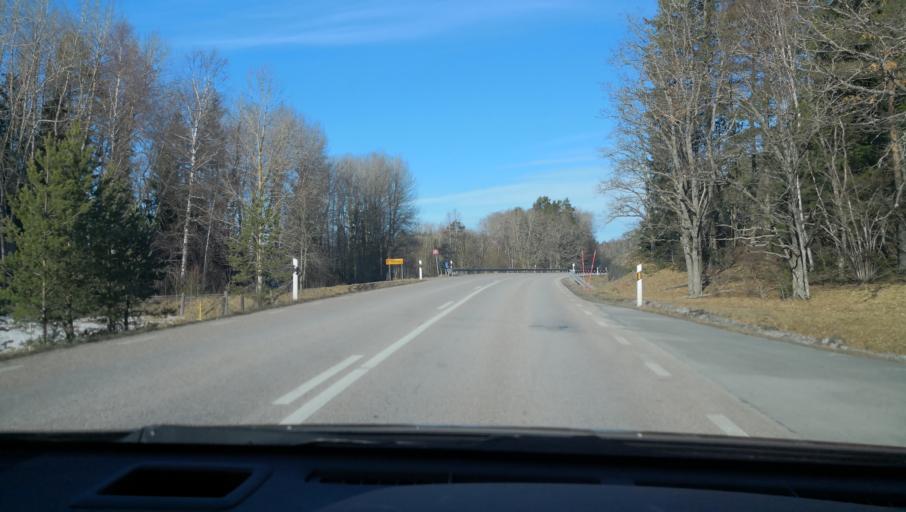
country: SE
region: Uppsala
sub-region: Osthammars Kommun
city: Osterbybruk
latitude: 60.1349
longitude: 17.8151
